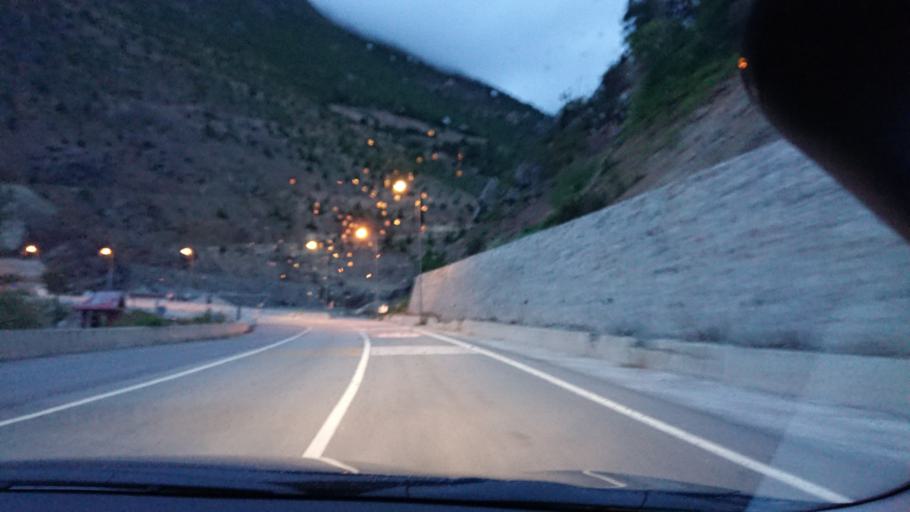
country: TR
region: Gumushane
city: Torul
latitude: 40.6323
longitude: 39.2399
